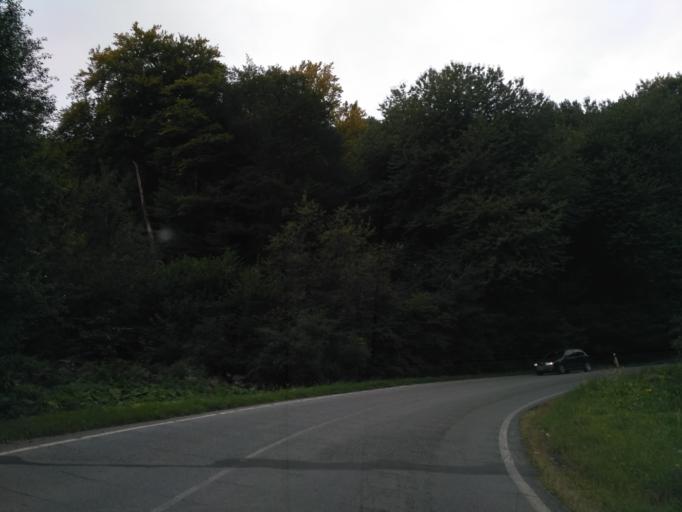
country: SK
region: Presovsky
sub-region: Okres Presov
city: Presov
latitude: 48.9863
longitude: 21.1894
